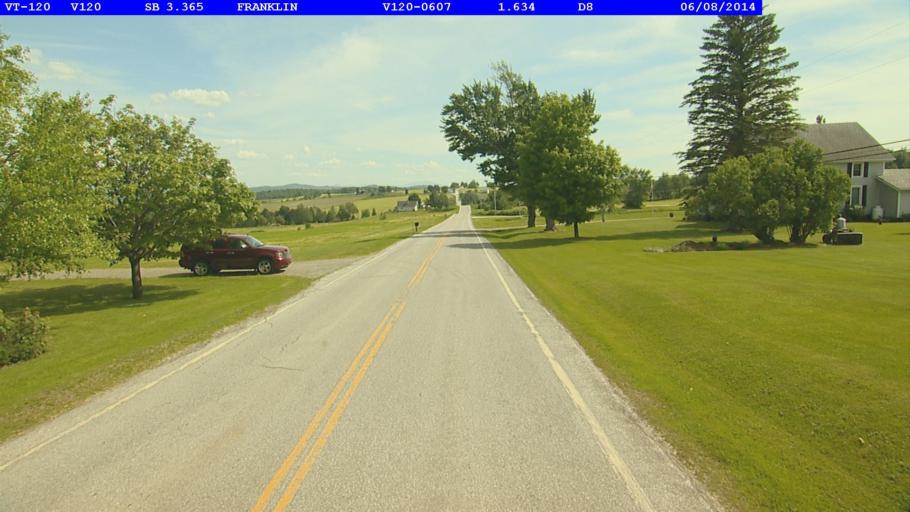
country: US
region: Vermont
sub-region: Franklin County
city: Enosburg Falls
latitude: 44.9566
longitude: -72.9060
